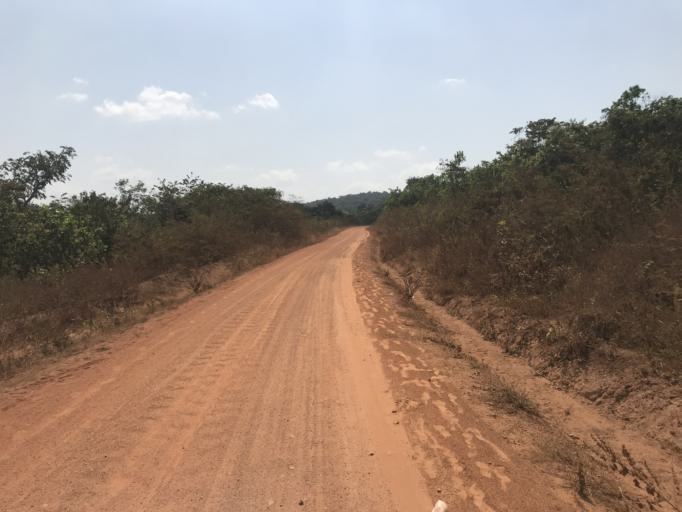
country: NG
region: Osun
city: Ifon
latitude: 7.9003
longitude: 4.4779
